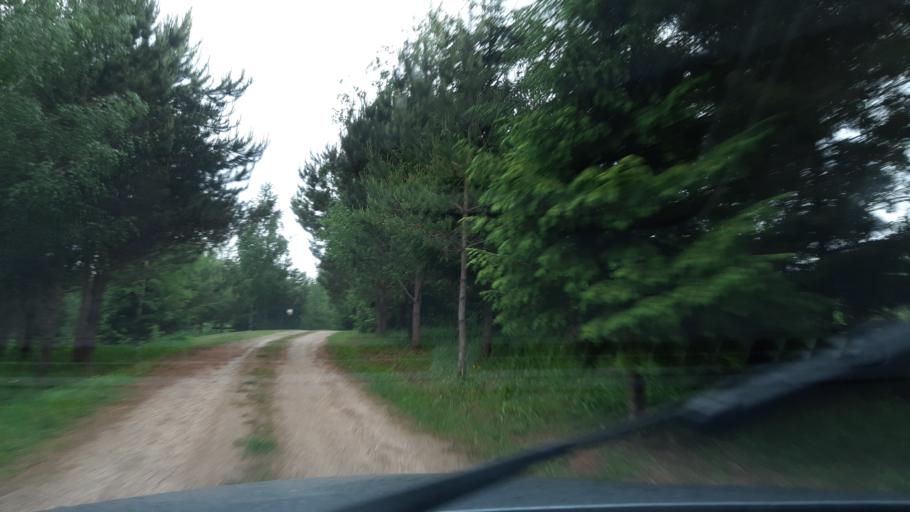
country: LT
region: Utenos apskritis
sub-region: Anyksciai
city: Anyksciai
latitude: 55.4464
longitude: 25.1953
